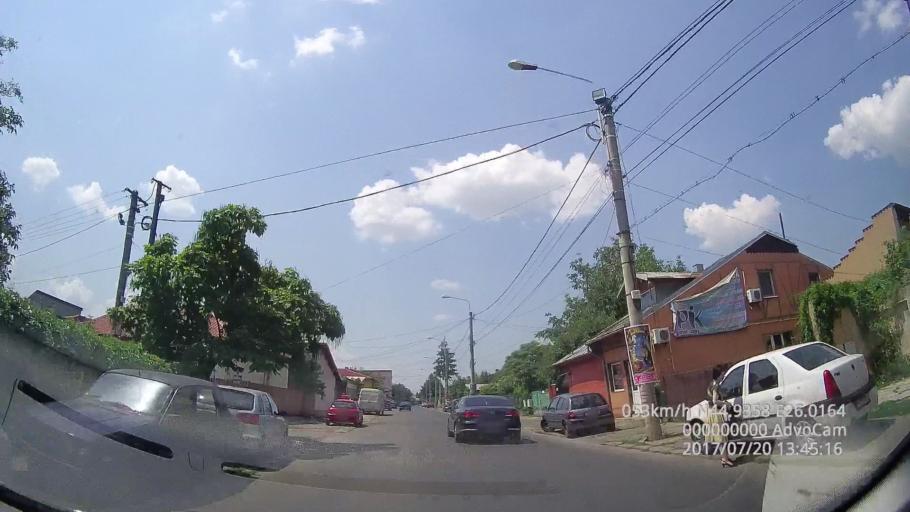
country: RO
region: Prahova
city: Ploiesti
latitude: 44.9357
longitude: 26.0161
